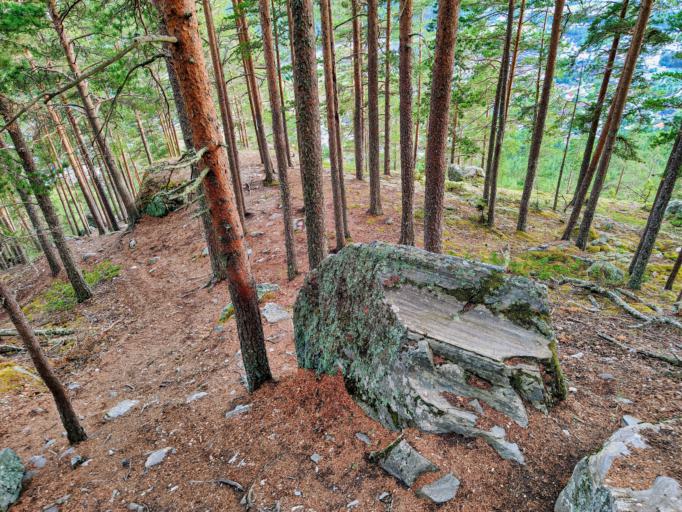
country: NO
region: Buskerud
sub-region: Gol
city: Gol
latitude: 60.7086
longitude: 8.9674
